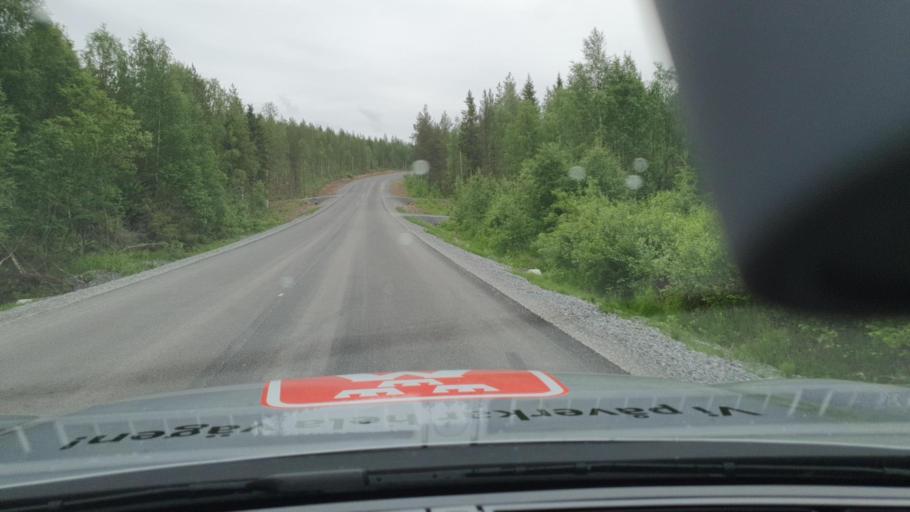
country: SE
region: Norrbotten
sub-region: Overtornea Kommun
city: OEvertornea
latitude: 66.6015
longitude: 23.3039
